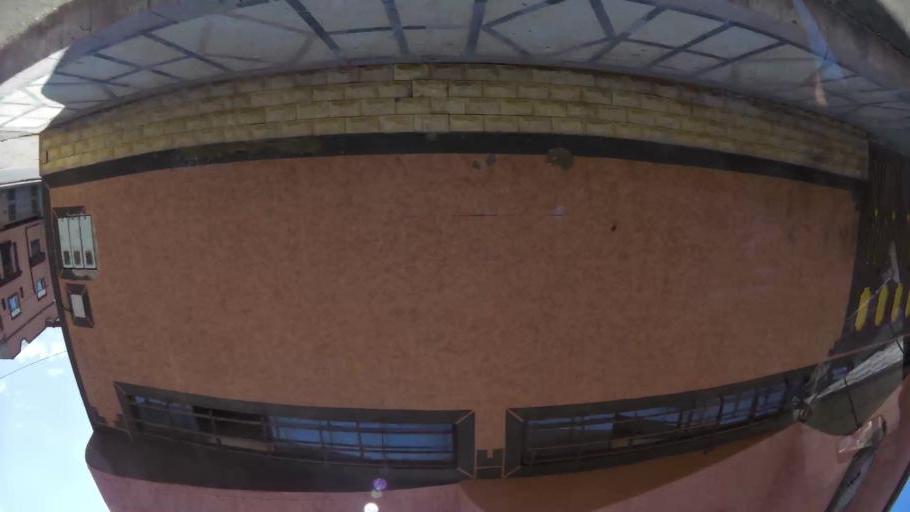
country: MA
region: Oriental
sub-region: Oujda-Angad
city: Oujda
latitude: 34.6865
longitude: -1.8904
